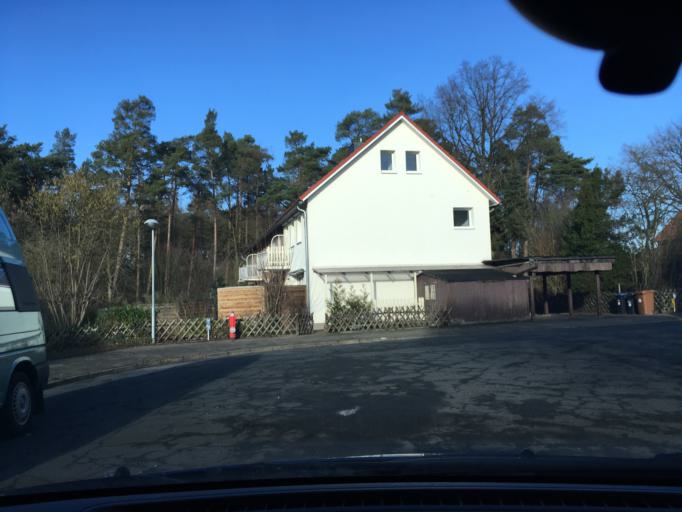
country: DE
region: Lower Saxony
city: Lueneburg
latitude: 53.2196
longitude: 10.4017
